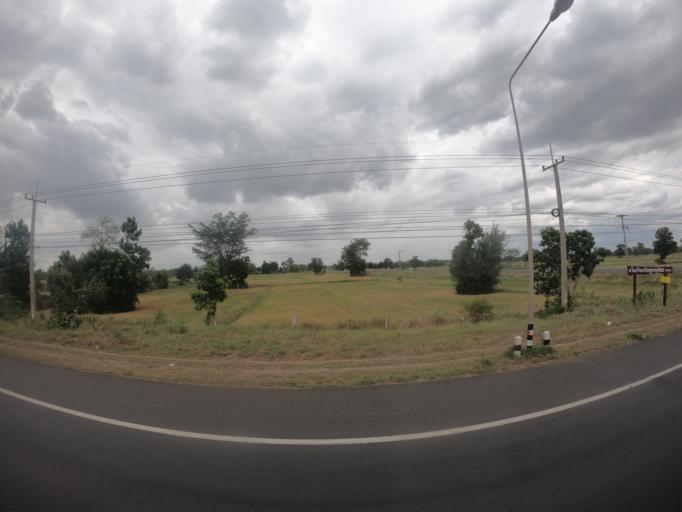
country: TH
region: Buriram
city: Nong Ki
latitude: 14.6700
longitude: 102.5901
